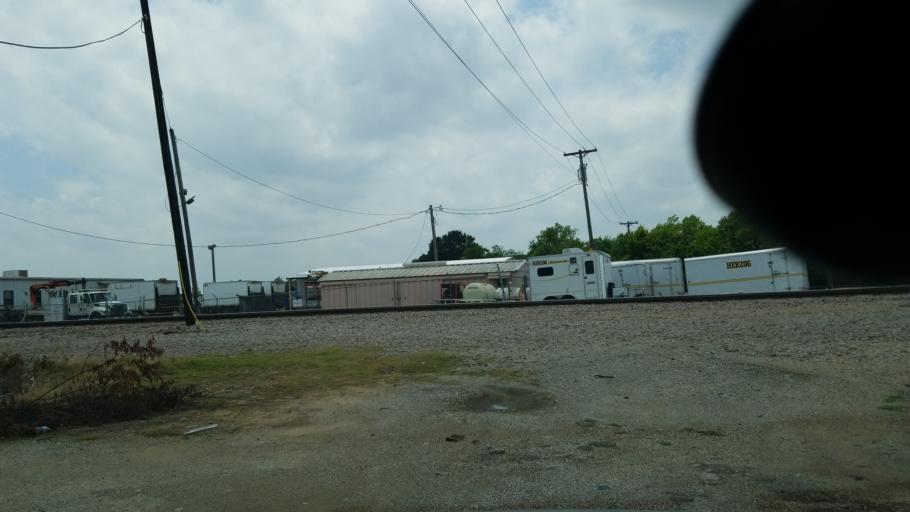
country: US
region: Texas
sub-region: Dallas County
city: Irving
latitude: 32.8169
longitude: -96.9456
